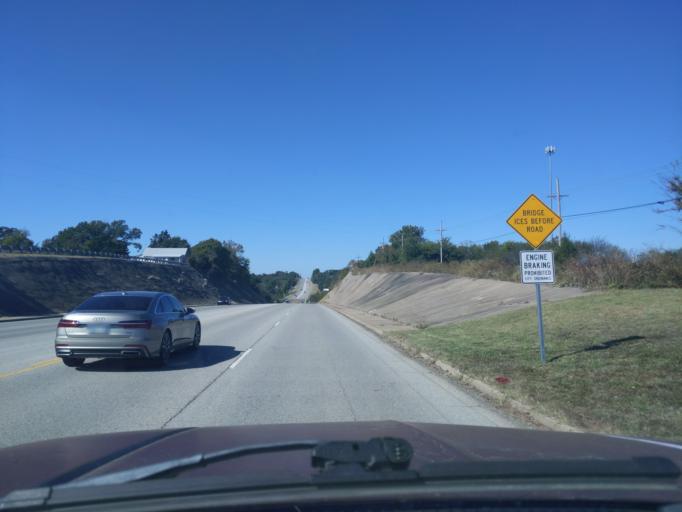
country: US
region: Oklahoma
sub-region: Creek County
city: Sapulpa
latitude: 35.9885
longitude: -96.0761
